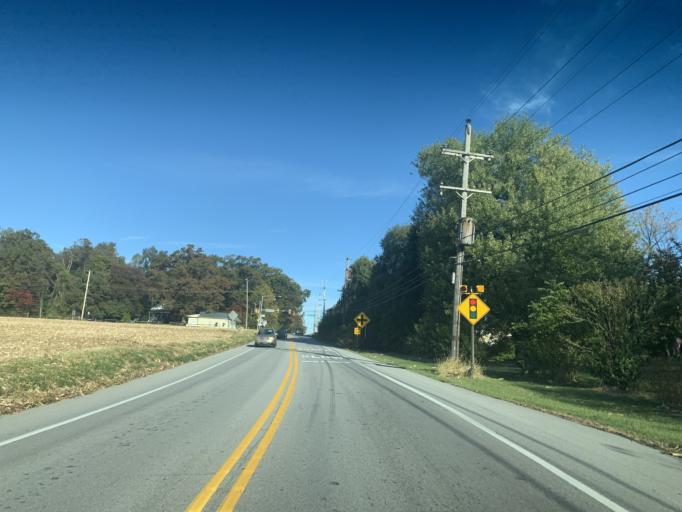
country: US
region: Pennsylvania
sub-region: Chester County
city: Parkesburg
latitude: 39.9377
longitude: -75.9101
